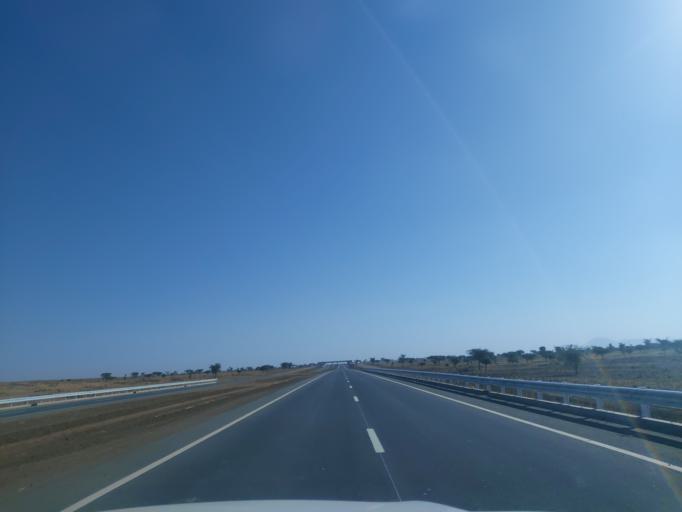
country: ET
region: Oromiya
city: Ziway
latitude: 8.1956
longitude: 38.8398
